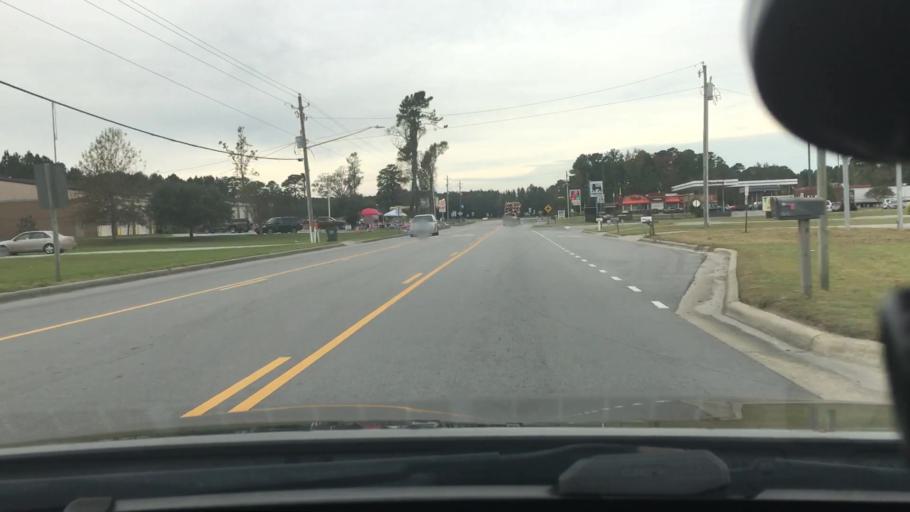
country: US
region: North Carolina
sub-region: Craven County
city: Vanceboro
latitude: 35.3097
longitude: -77.1590
